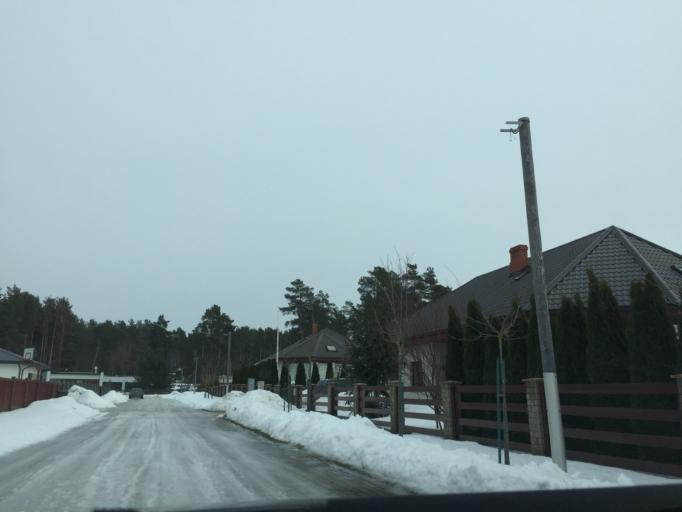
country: LV
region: Ikskile
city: Ikskile
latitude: 56.8368
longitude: 24.4817
